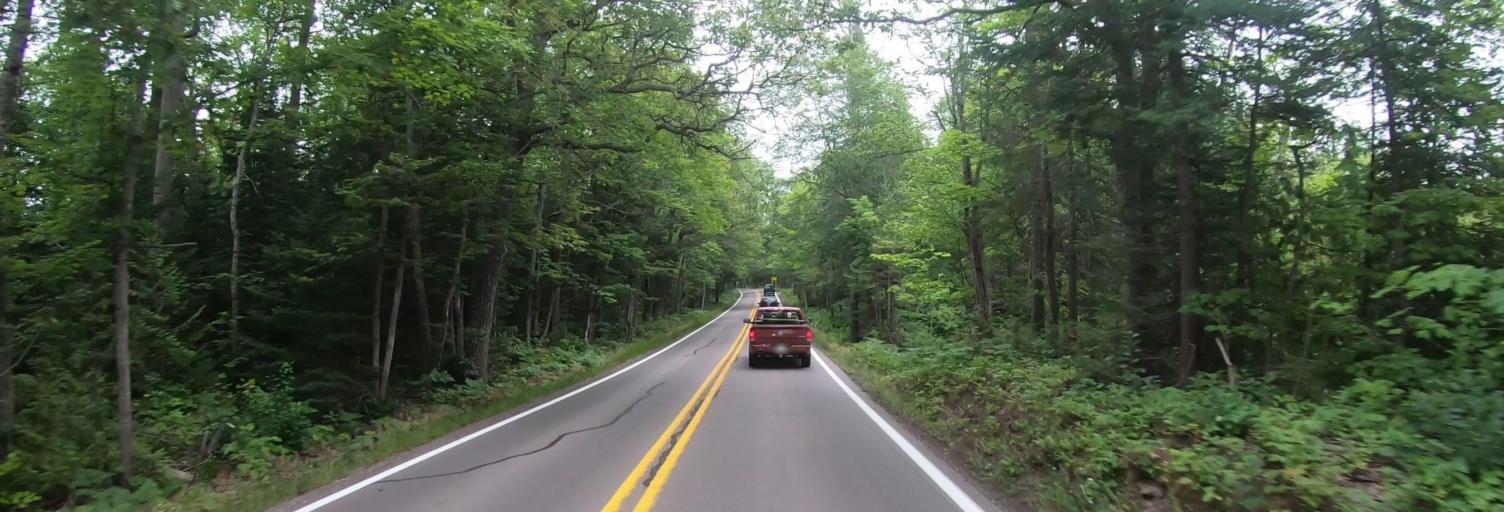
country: US
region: Michigan
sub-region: Keweenaw County
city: Eagle River
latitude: 47.4383
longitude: -87.9577
